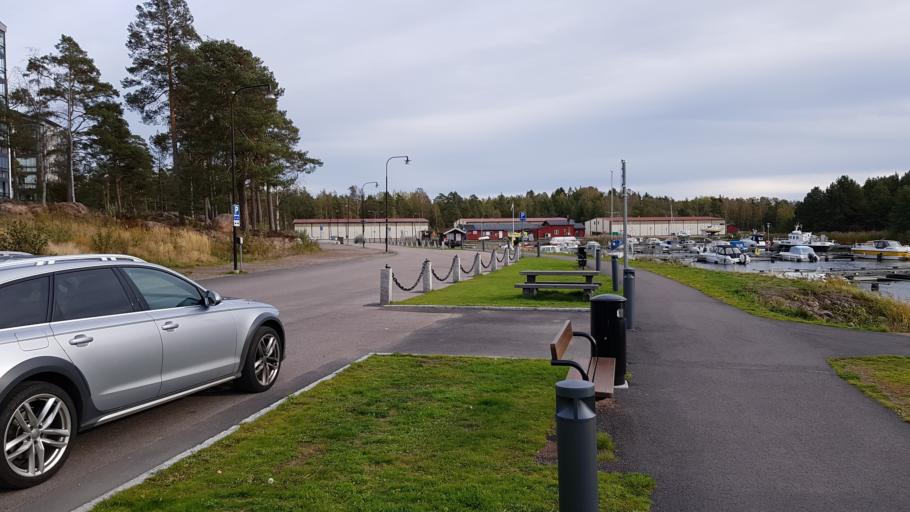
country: SE
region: Vaermland
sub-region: Hammaro Kommun
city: Skoghall
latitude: 59.3177
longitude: 13.4642
